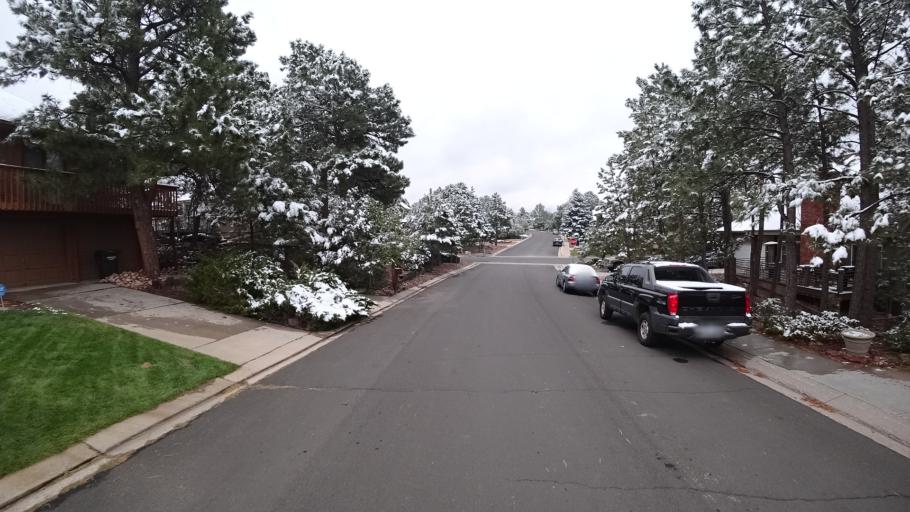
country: US
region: Colorado
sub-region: El Paso County
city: Colorado Springs
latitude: 38.9173
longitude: -104.7927
